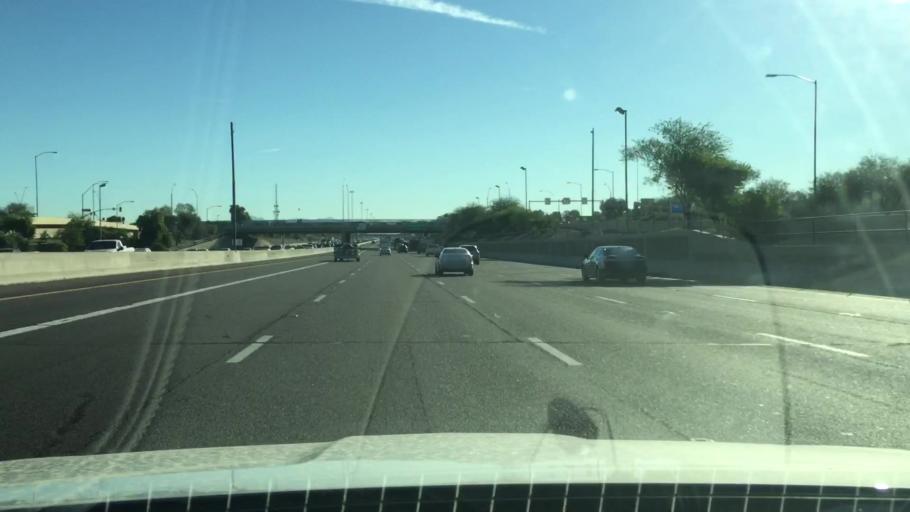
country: US
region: Arizona
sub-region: Maricopa County
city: Tempe
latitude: 33.3853
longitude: -111.8776
